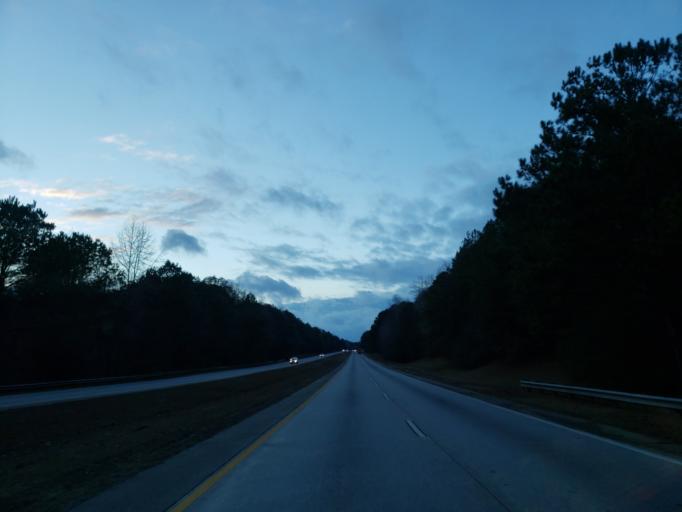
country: US
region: Georgia
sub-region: Fulton County
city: Union City
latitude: 33.6820
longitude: -84.5558
